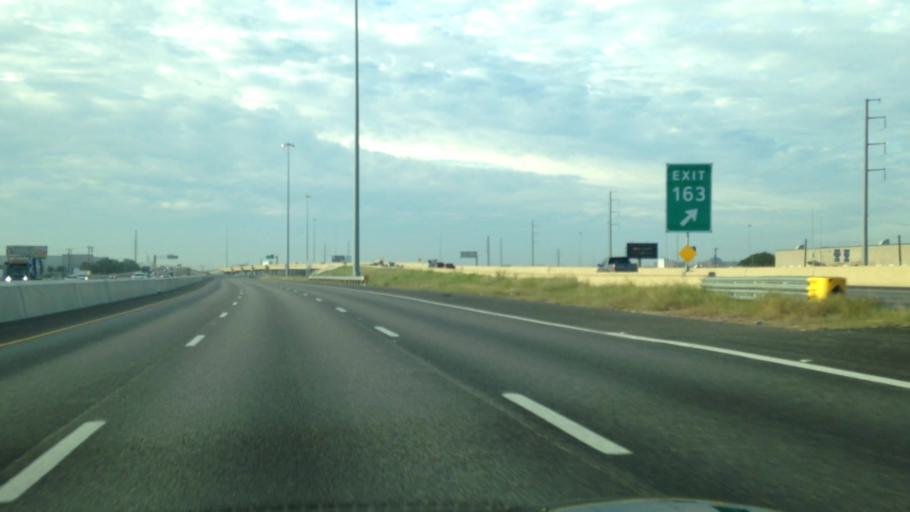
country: US
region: Texas
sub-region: Bexar County
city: Kirby
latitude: 29.4785
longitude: -98.4048
